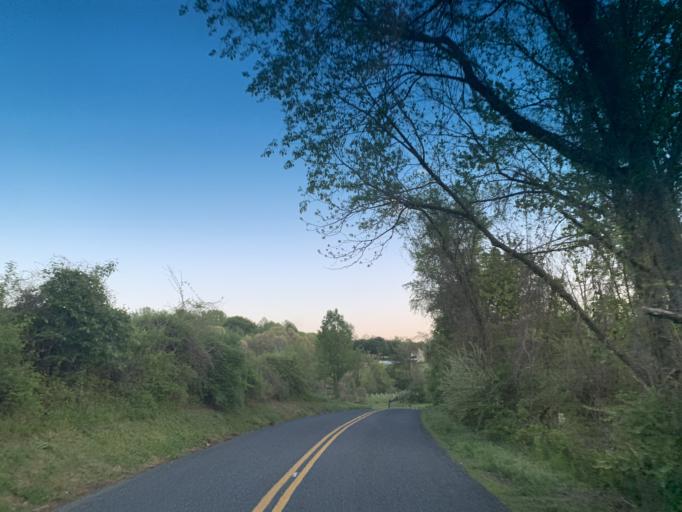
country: US
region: Maryland
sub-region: Harford County
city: Bel Air South
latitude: 39.5380
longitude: -76.2762
